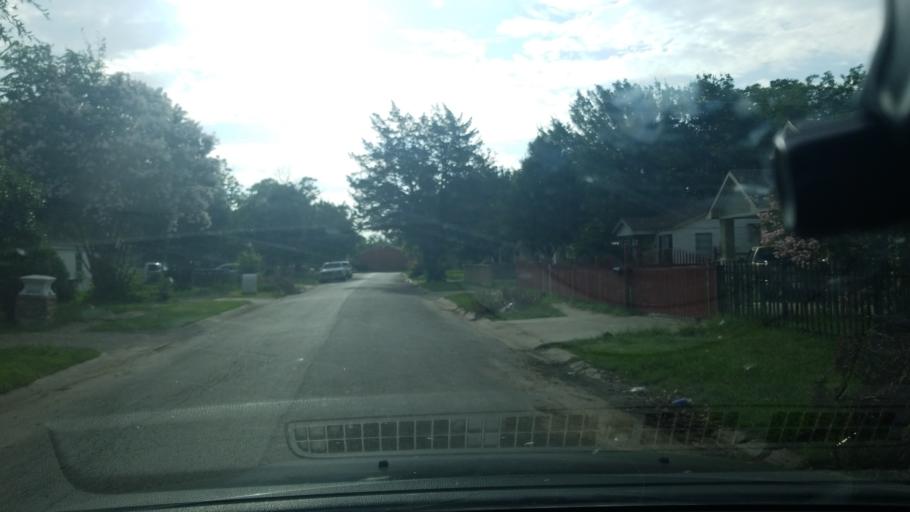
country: US
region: Texas
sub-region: Dallas County
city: Balch Springs
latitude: 32.7378
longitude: -96.6672
